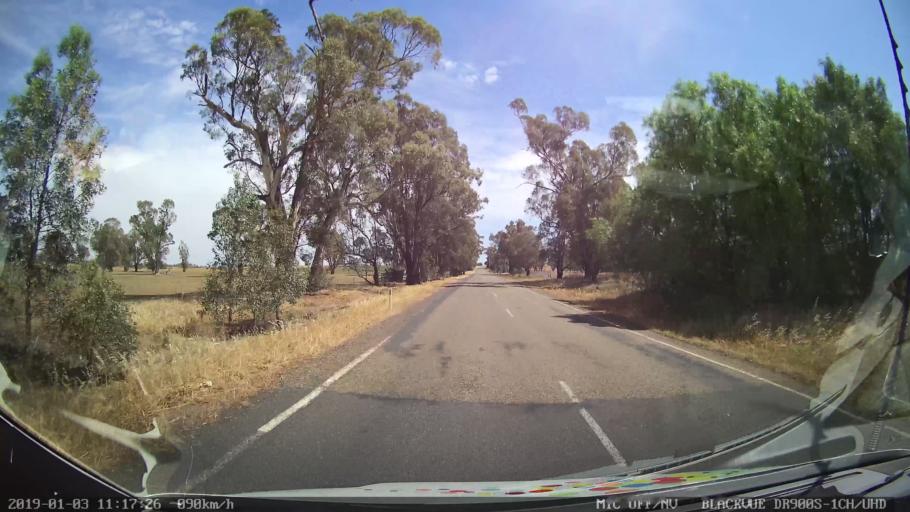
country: AU
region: New South Wales
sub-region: Young
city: Young
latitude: -34.1388
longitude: 148.2659
